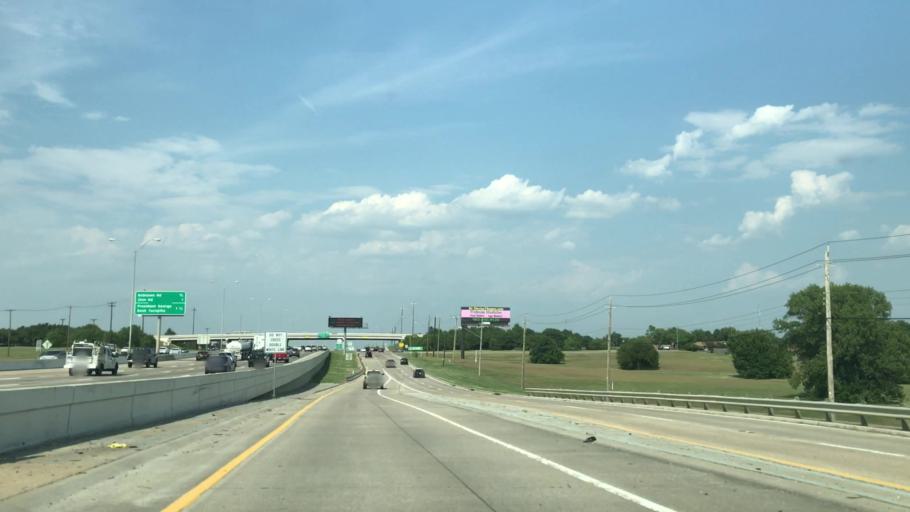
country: US
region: Texas
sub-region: Dallas County
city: Sunnyvale
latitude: 32.8436
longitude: -96.5862
